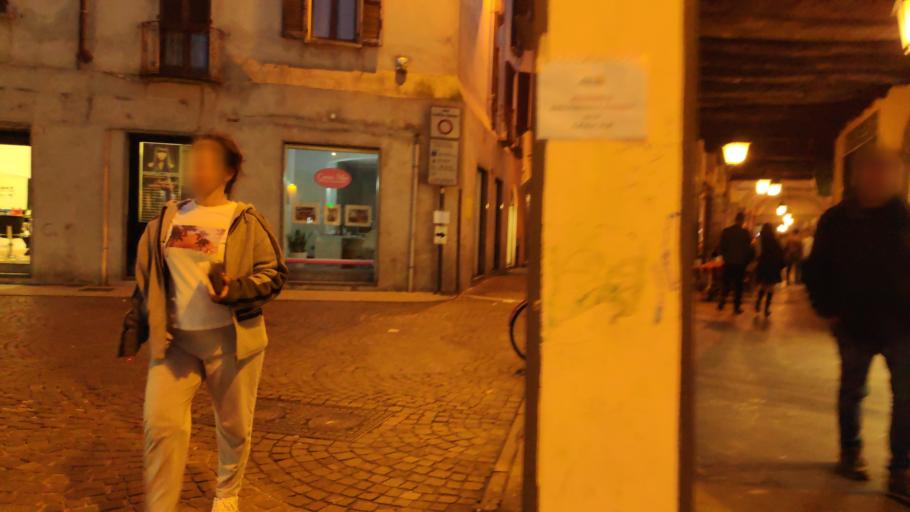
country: IT
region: Lombardy
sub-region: Citta metropolitana di Milano
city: Abbiategrasso
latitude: 45.3992
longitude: 8.9166
